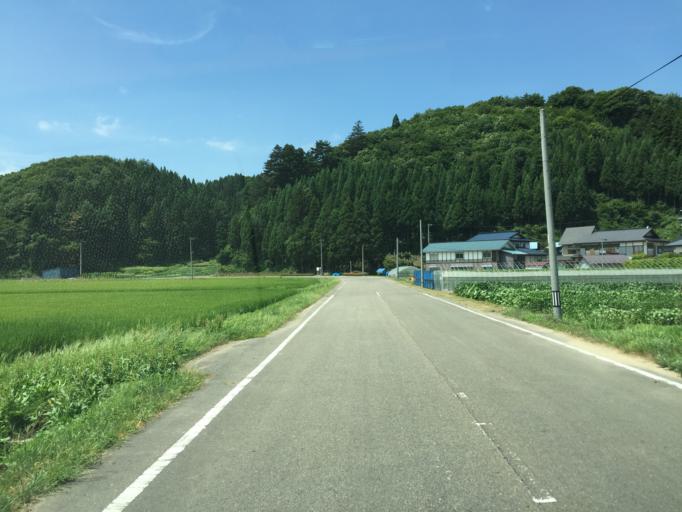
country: JP
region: Fukushima
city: Inawashiro
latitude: 37.4678
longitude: 140.0412
